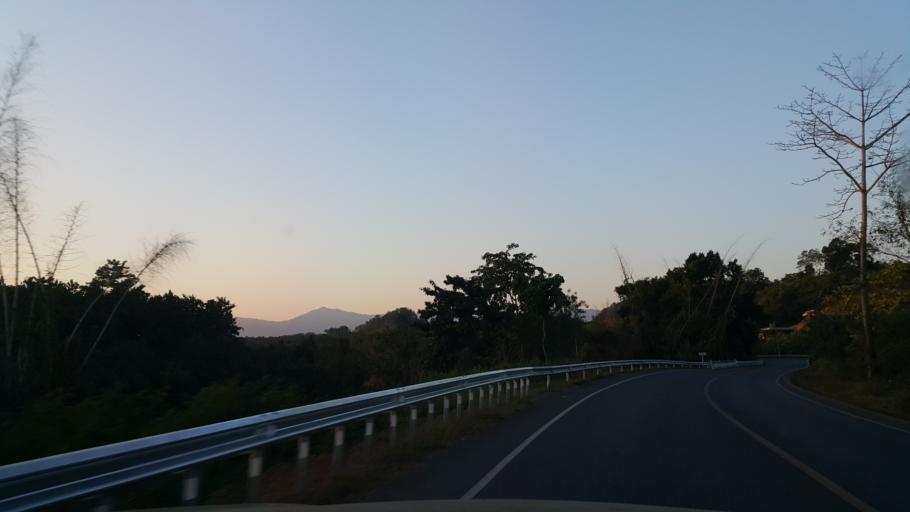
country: TH
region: Phrae
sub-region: Amphoe Wang Chin
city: Wang Chin
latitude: 17.8457
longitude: 99.6409
